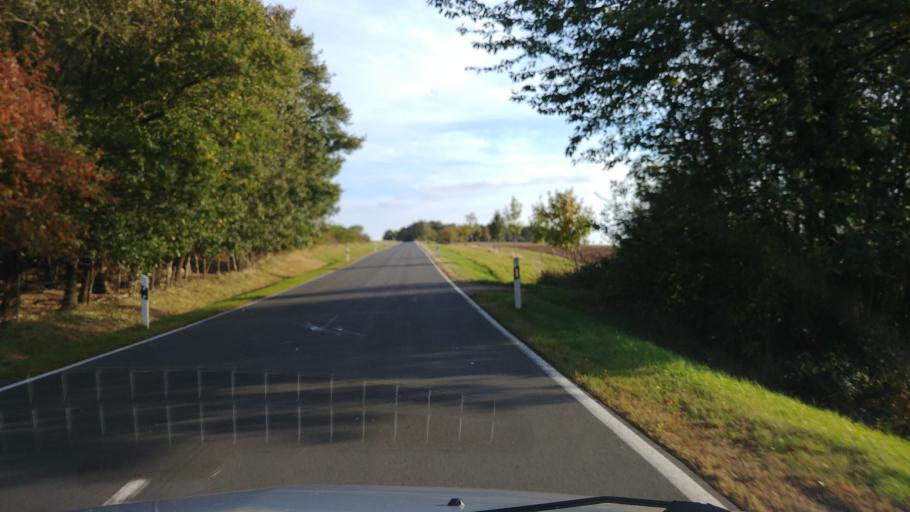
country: DE
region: Rheinland-Pfalz
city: Merschbach
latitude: 49.8209
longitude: 7.0329
